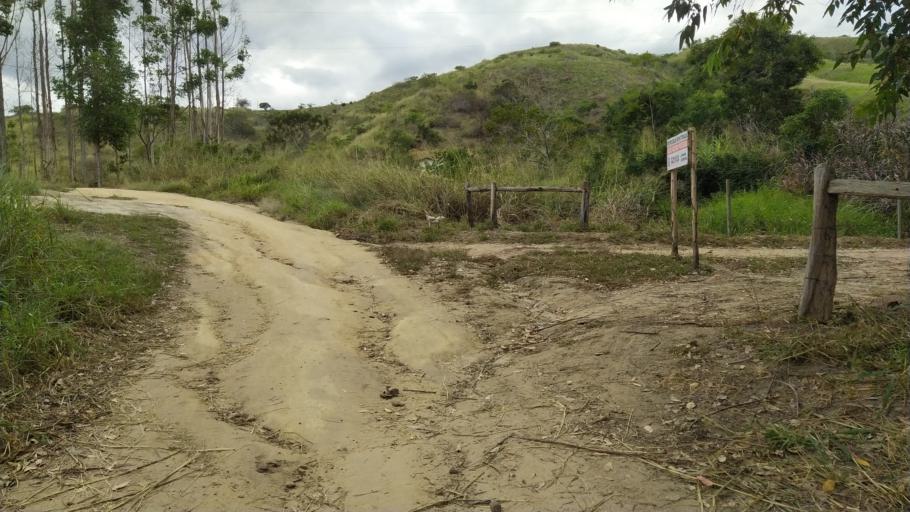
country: BR
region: Minas Gerais
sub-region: Almenara
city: Almenara
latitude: -16.6293
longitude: -40.4575
